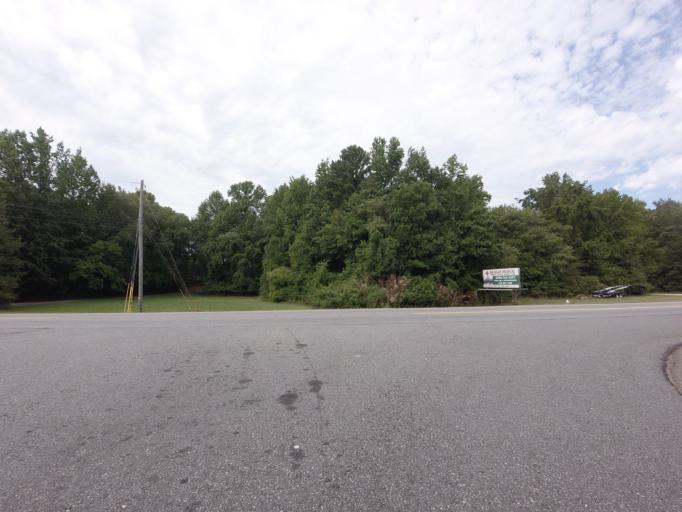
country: US
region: Georgia
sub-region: Gwinnett County
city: Duluth
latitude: 34.0250
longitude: -84.1647
